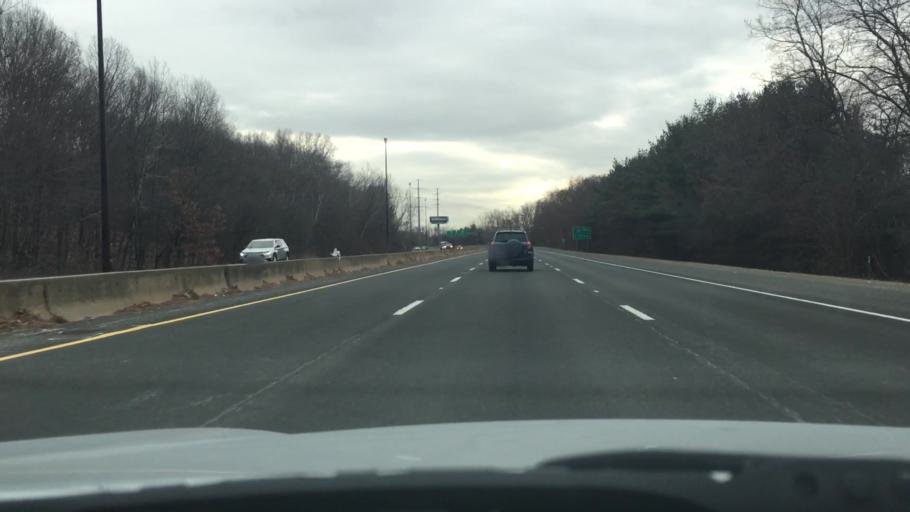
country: US
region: Massachusetts
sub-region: Hampden County
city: Chicopee
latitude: 42.1653
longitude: -72.6112
